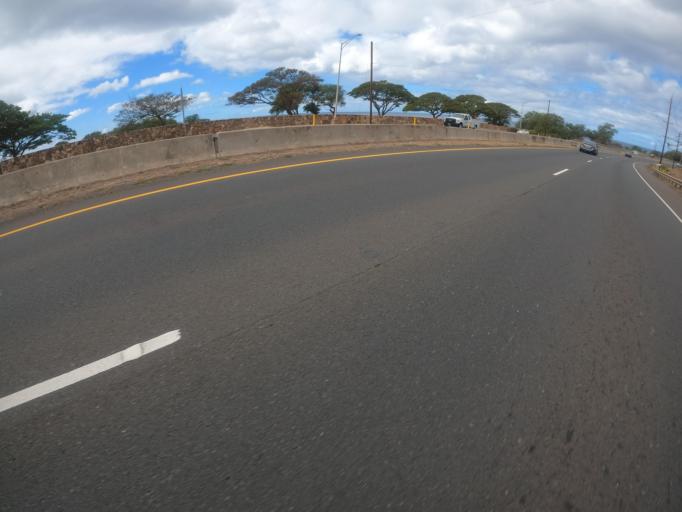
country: US
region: Hawaii
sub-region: Honolulu County
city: Makakilo
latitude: 21.3482
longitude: -158.1273
